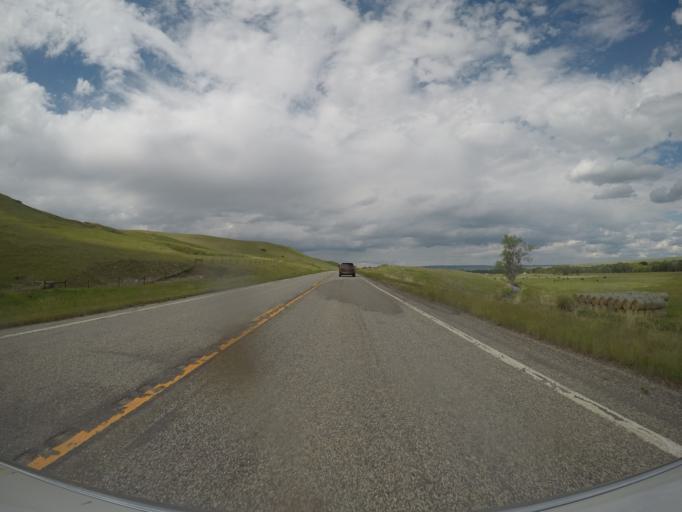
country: US
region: Montana
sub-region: Sweet Grass County
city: Big Timber
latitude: 45.7997
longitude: -109.9692
